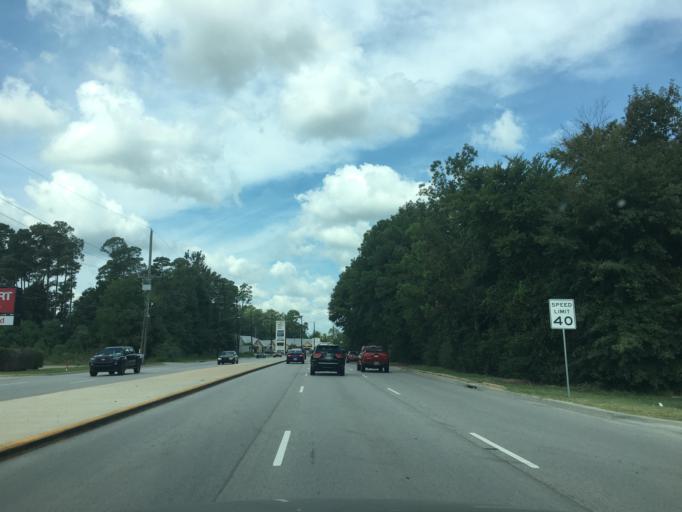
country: US
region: Texas
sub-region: Montgomery County
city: Oak Ridge North
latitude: 30.1259
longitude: -95.4216
